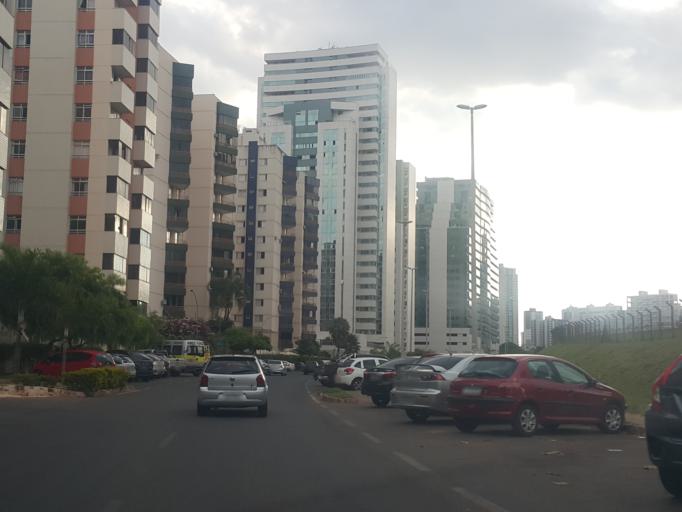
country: BR
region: Federal District
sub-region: Brasilia
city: Brasilia
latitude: -15.8401
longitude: -48.0240
